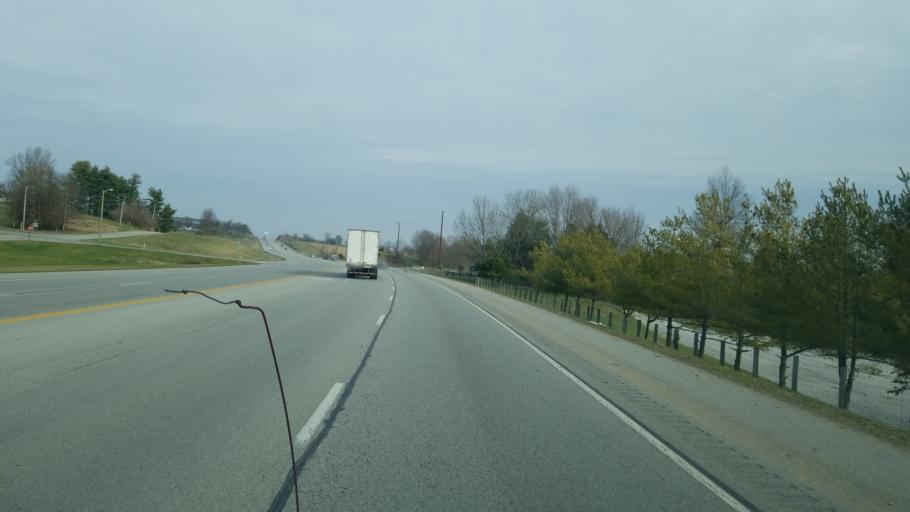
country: US
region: Kentucky
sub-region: Boyle County
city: Junction City
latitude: 37.6001
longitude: -84.7738
